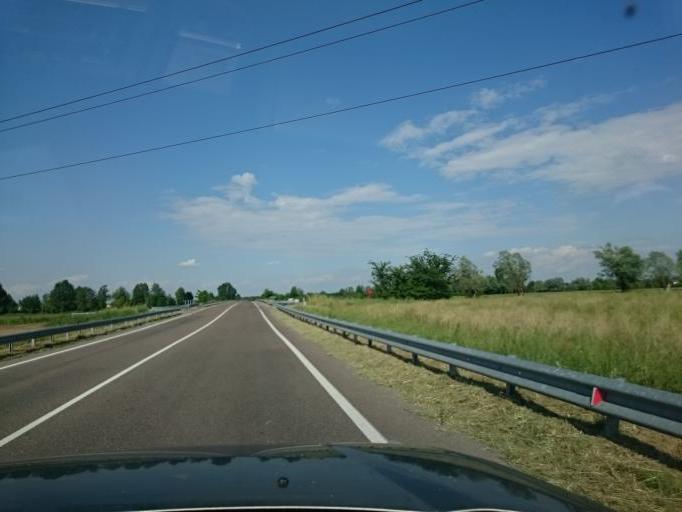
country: IT
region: Veneto
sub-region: Provincia di Vicenza
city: Grisignano di Zocco
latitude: 45.4692
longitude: 11.7002
